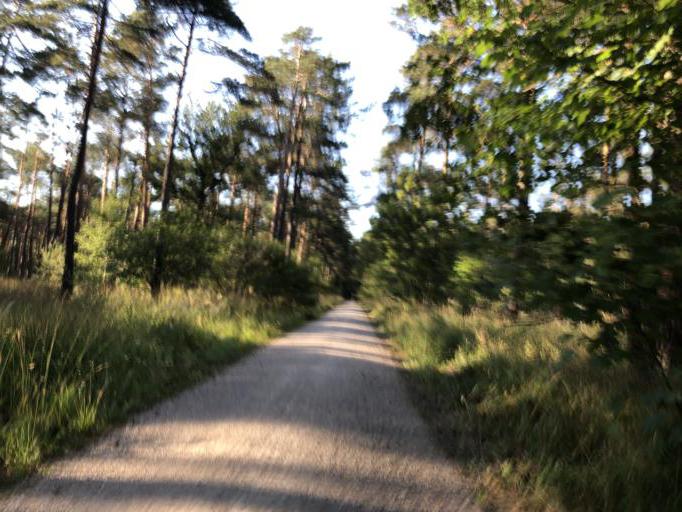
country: DE
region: Bavaria
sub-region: Regierungsbezirk Mittelfranken
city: Kalchreuth
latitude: 49.5565
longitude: 11.0975
